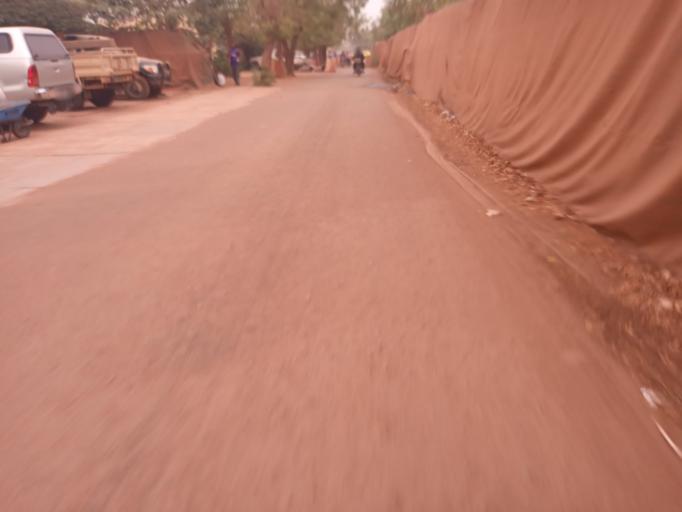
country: ML
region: Bamako
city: Bamako
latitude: 12.5963
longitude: -7.9593
